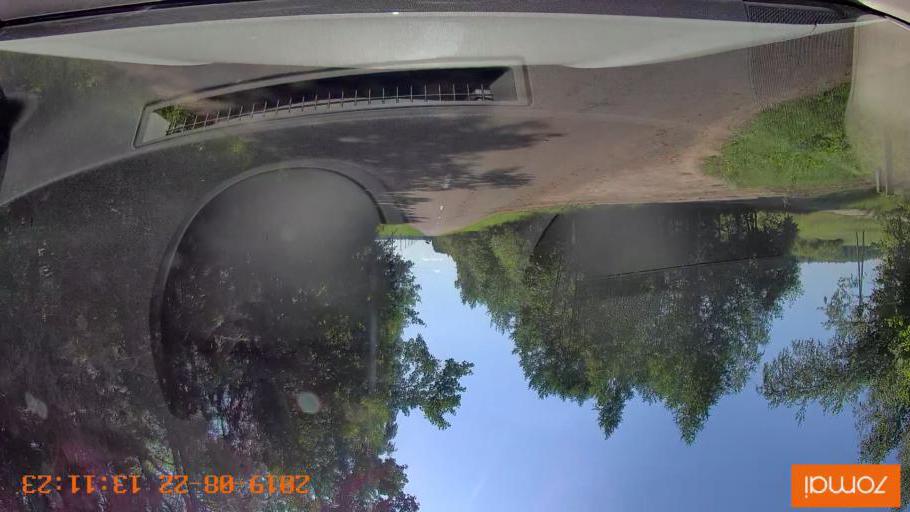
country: BY
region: Minsk
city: Prawdzinski
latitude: 53.2815
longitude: 27.8527
